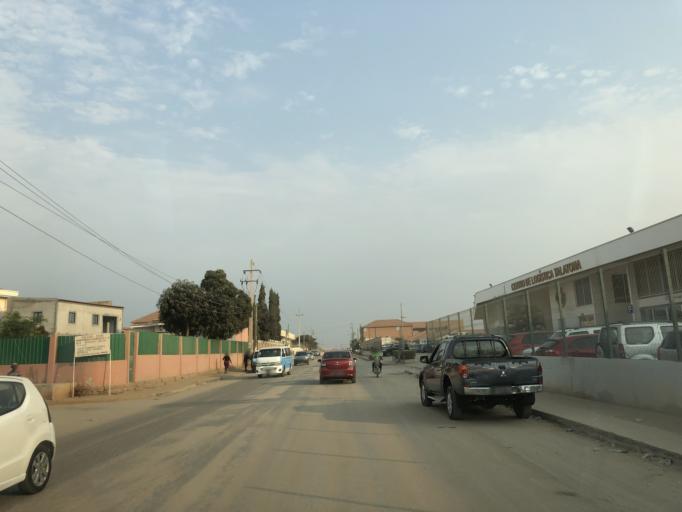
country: AO
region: Luanda
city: Luanda
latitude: -8.9085
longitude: 13.2075
